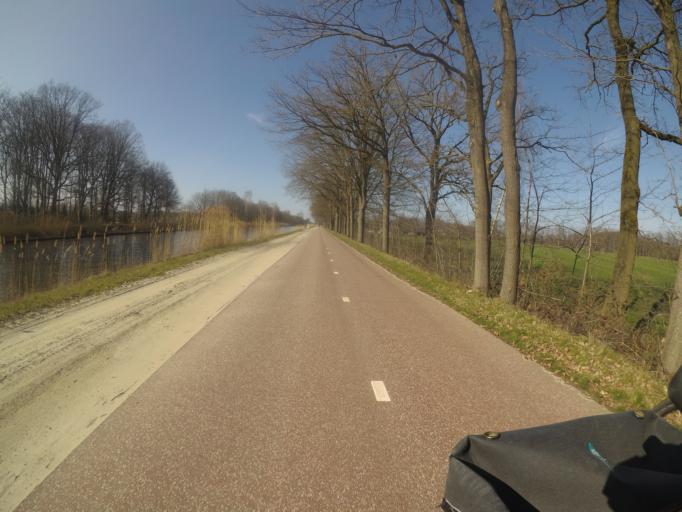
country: NL
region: North Brabant
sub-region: Gemeente Tilburg
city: Tilburg
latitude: 51.5399
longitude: 5.1225
